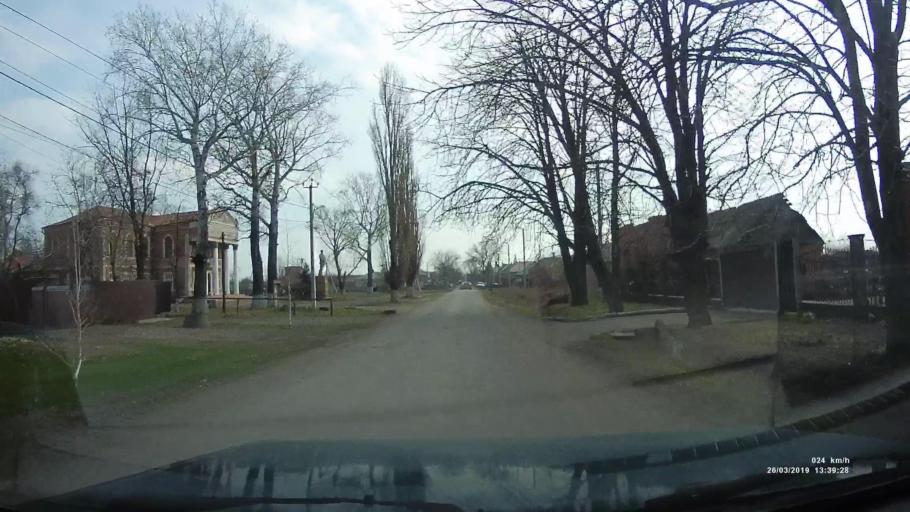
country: RU
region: Rostov
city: Novobessergenovka
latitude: 47.1834
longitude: 38.8425
